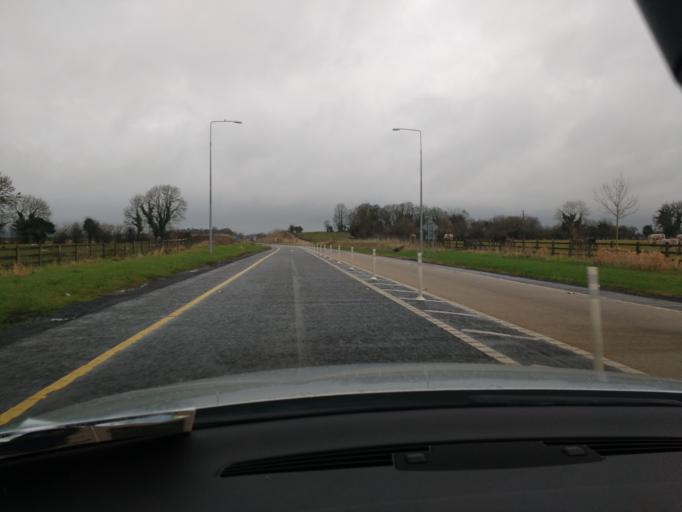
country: IE
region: Munster
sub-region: North Tipperary
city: Nenagh
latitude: 52.8484
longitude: -8.1557
